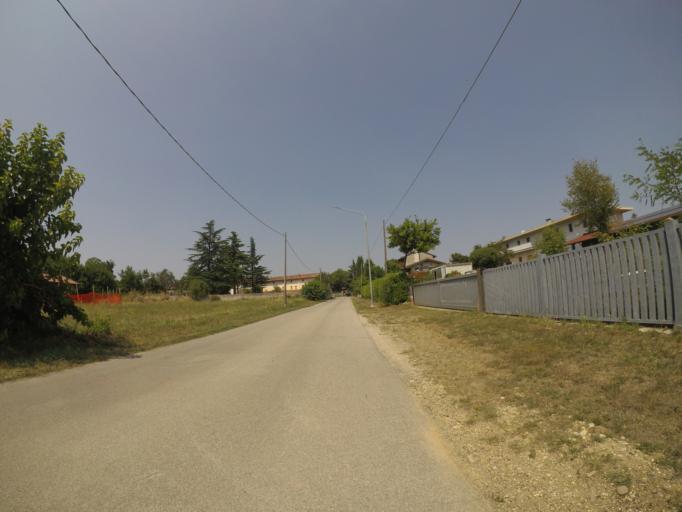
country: IT
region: Friuli Venezia Giulia
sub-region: Provincia di Udine
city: Talmassons
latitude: 45.9270
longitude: 13.1235
